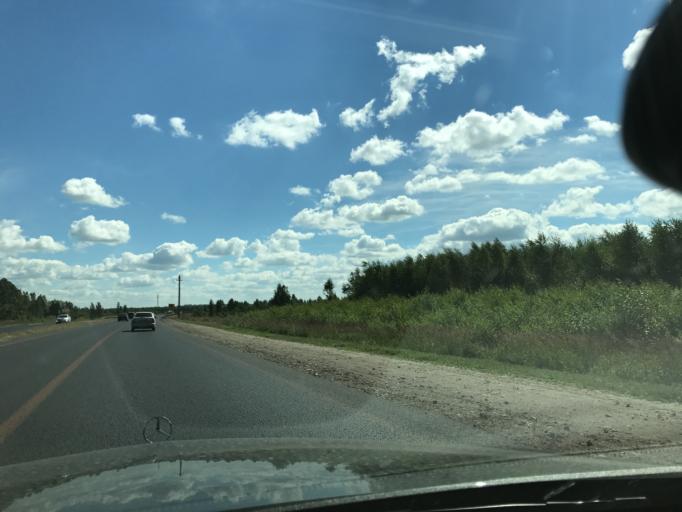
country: RU
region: Nizjnij Novgorod
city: Gorbatovka
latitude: 56.2298
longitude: 43.7453
